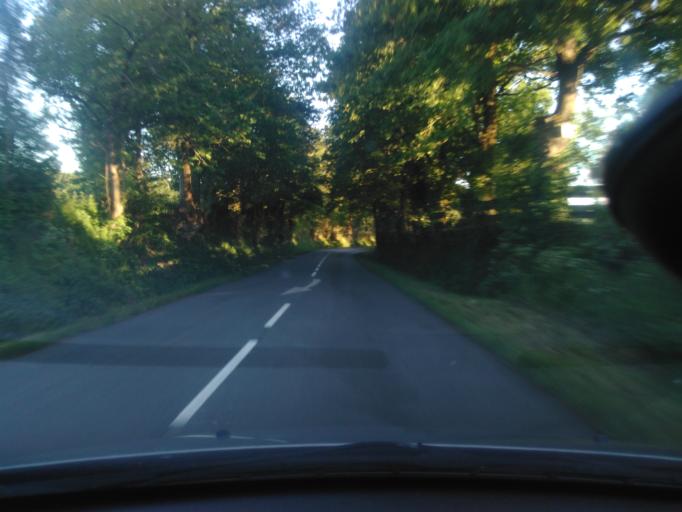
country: FR
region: Pays de la Loire
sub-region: Departement de la Vendee
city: Nesmy
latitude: 46.6228
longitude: -1.4081
